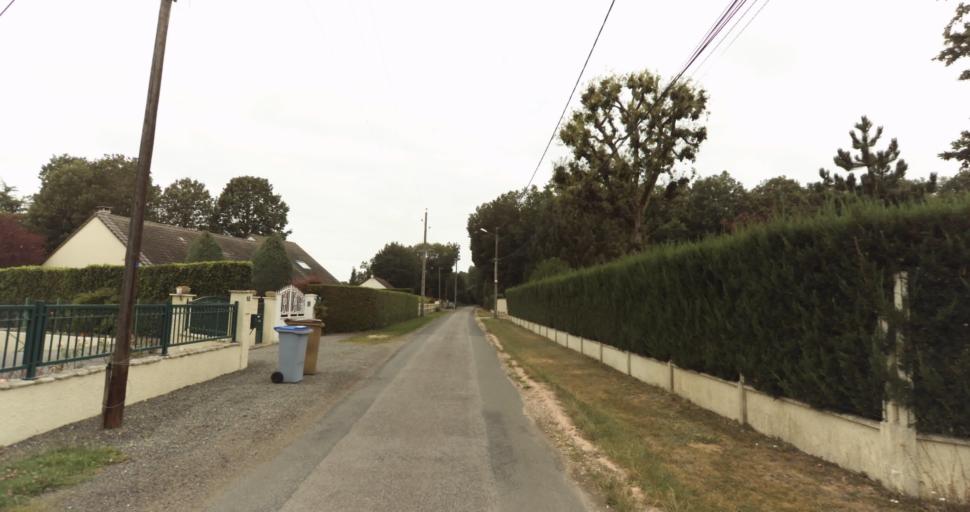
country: FR
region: Centre
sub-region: Departement d'Eure-et-Loir
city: Vert-en-Drouais
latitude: 48.7966
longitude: 1.2891
